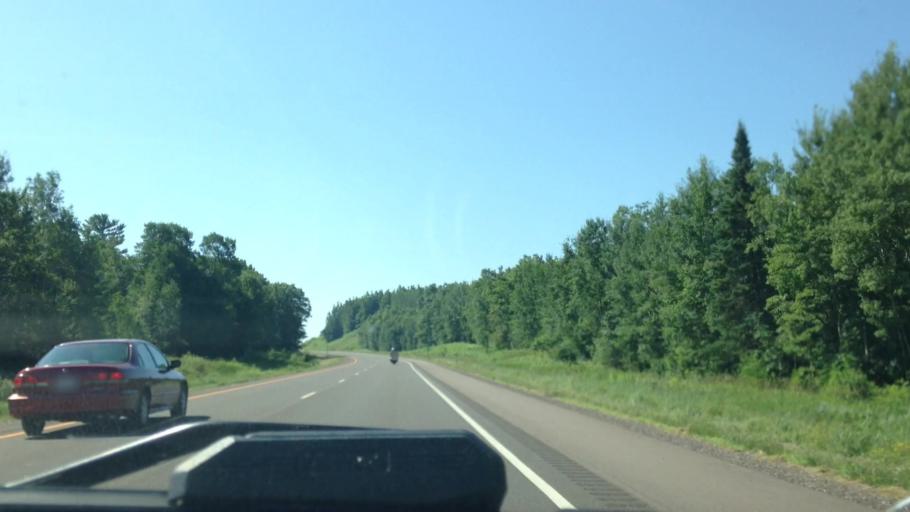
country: US
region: Wisconsin
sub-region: Washburn County
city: Spooner
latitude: 46.0124
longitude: -91.8372
